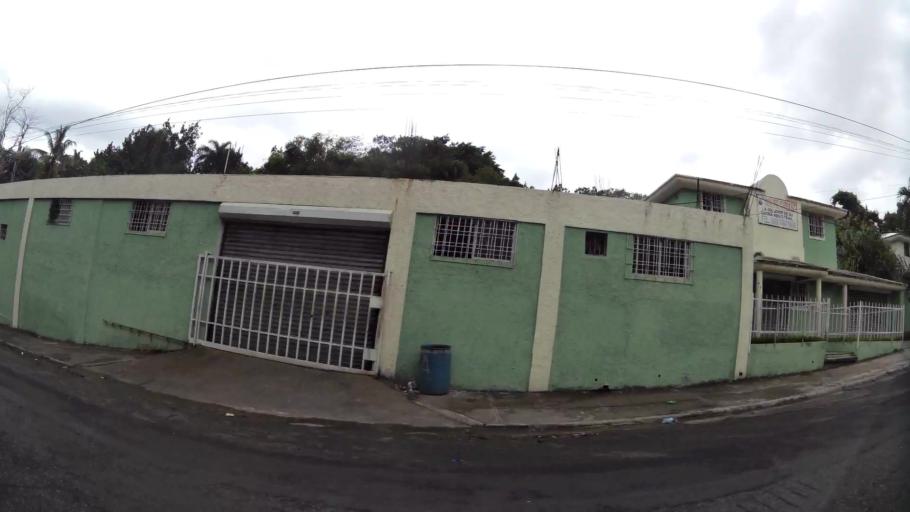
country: DO
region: Nacional
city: La Agustina
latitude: 18.5049
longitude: -69.9326
